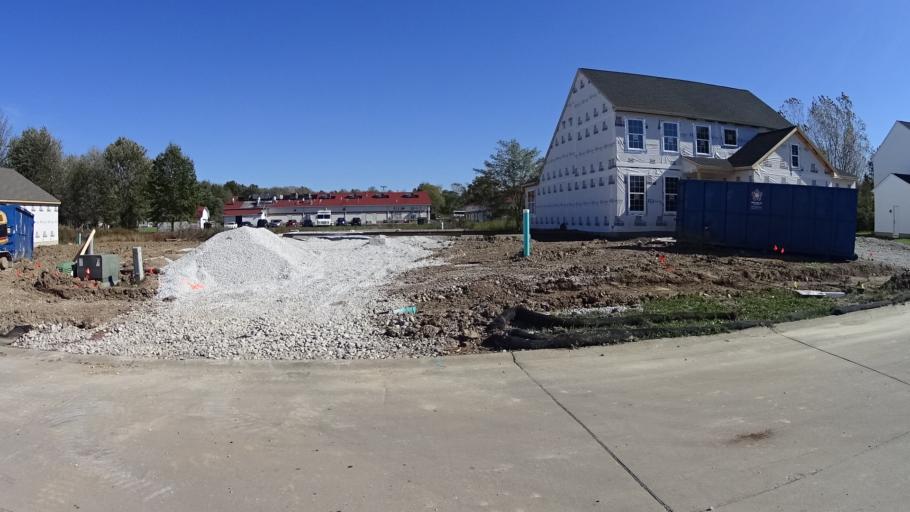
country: US
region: Ohio
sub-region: Lorain County
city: Amherst
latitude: 41.3843
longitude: -82.2126
